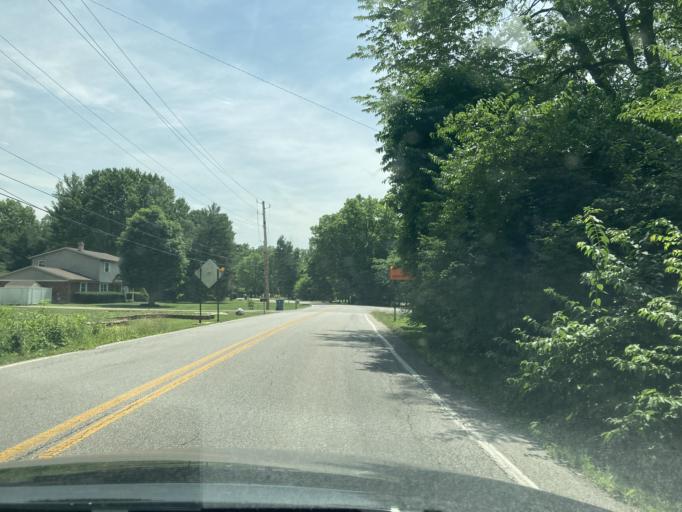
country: US
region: Indiana
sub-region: Marion County
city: Meridian Hills
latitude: 39.8645
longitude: -86.1790
